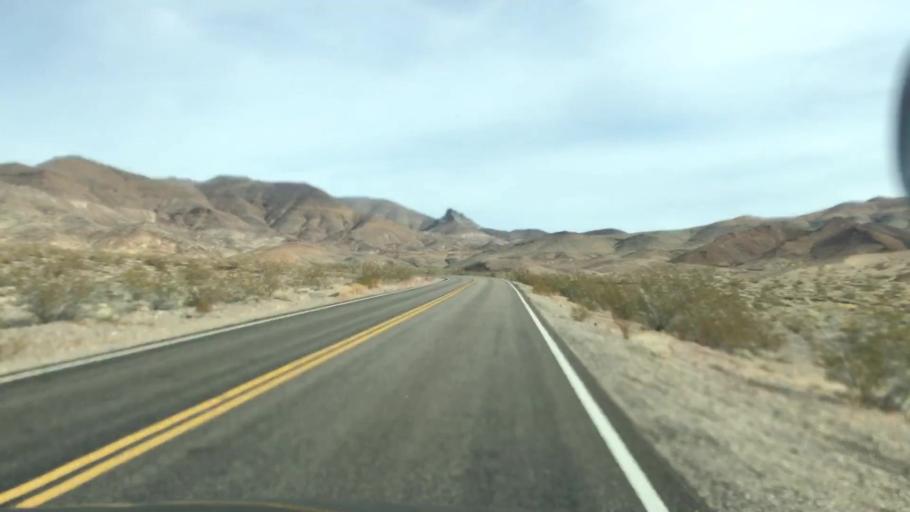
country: US
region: Nevada
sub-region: Nye County
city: Beatty
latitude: 36.7283
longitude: -116.9747
